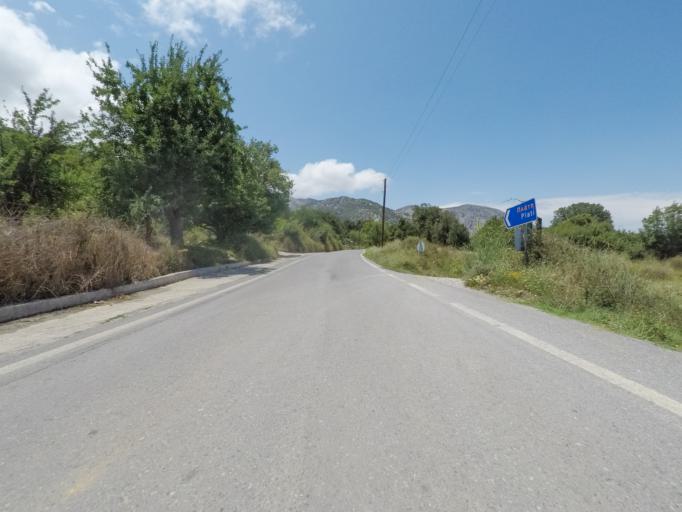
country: GR
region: Crete
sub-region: Nomos Irakleiou
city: Mokhos
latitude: 35.1680
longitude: 25.4477
